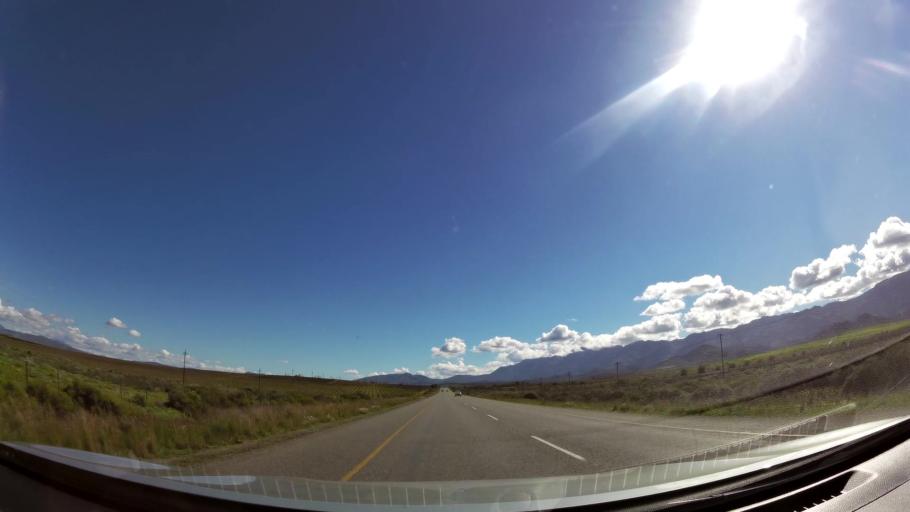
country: ZA
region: Western Cape
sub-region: Cape Winelands District Municipality
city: Ashton
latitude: -33.8327
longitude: 19.9971
